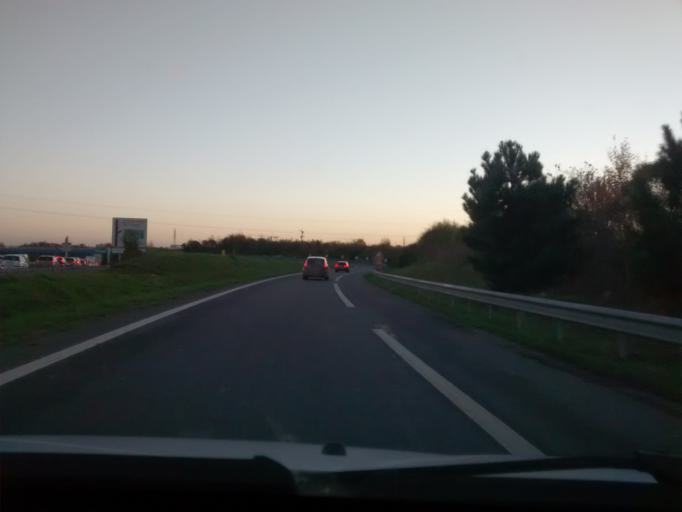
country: FR
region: Brittany
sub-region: Departement d'Ille-et-Vilaine
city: Saint-Gregoire
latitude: 48.1460
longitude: -1.6990
